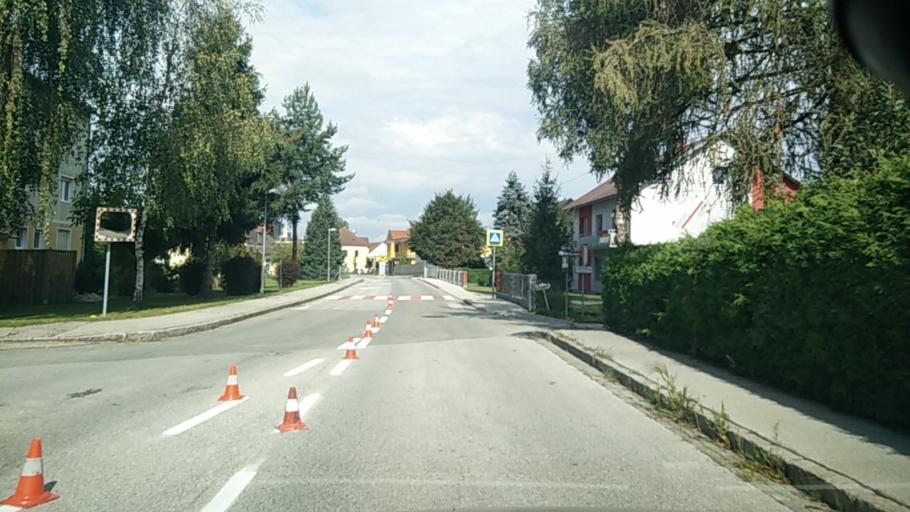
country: AT
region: Carinthia
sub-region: Politischer Bezirk Klagenfurt Land
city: Grafenstein
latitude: 46.6165
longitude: 14.4678
